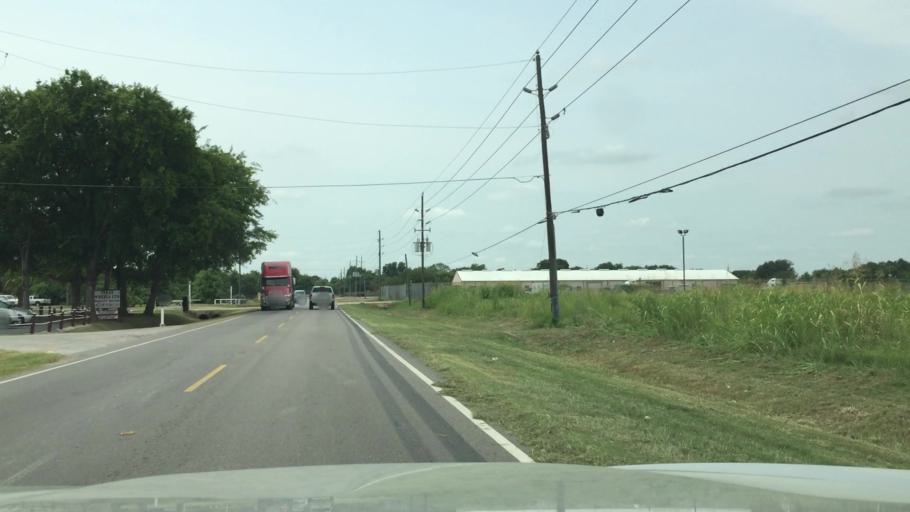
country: US
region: Texas
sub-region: Harris County
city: Jersey Village
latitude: 29.9216
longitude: -95.5480
